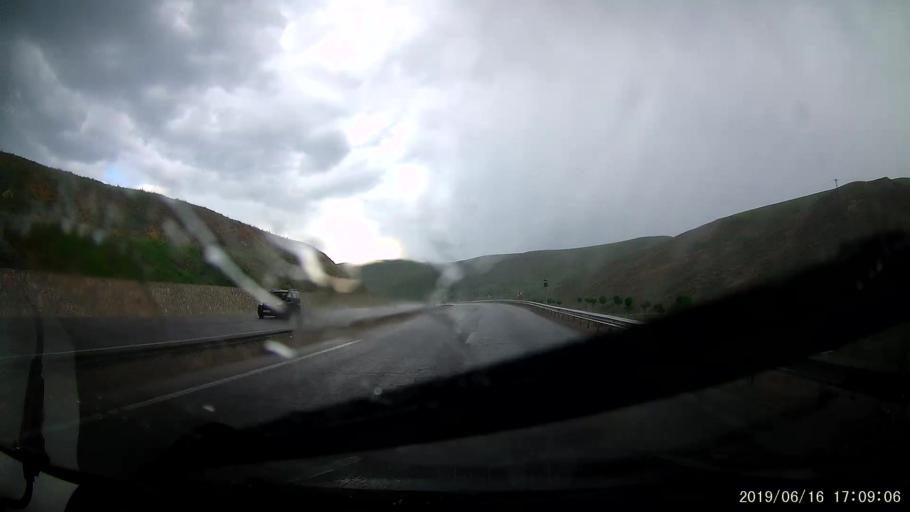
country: TR
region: Erzurum
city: Askale
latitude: 39.8995
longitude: 40.6536
